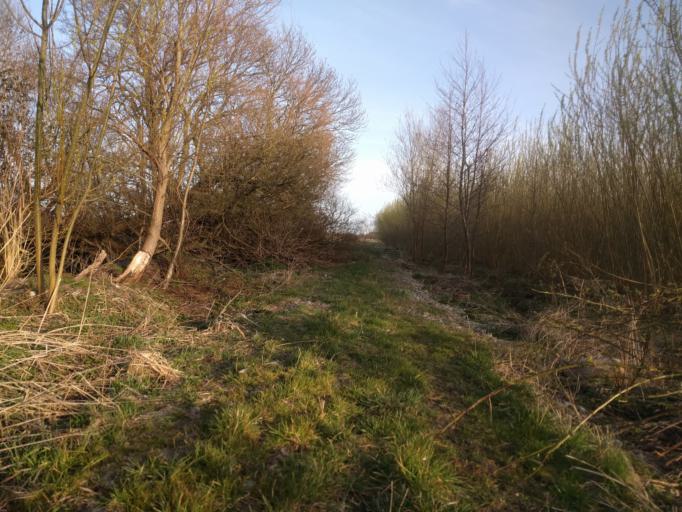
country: DK
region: South Denmark
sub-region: Kerteminde Kommune
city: Munkebo
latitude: 55.4118
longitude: 10.5505
